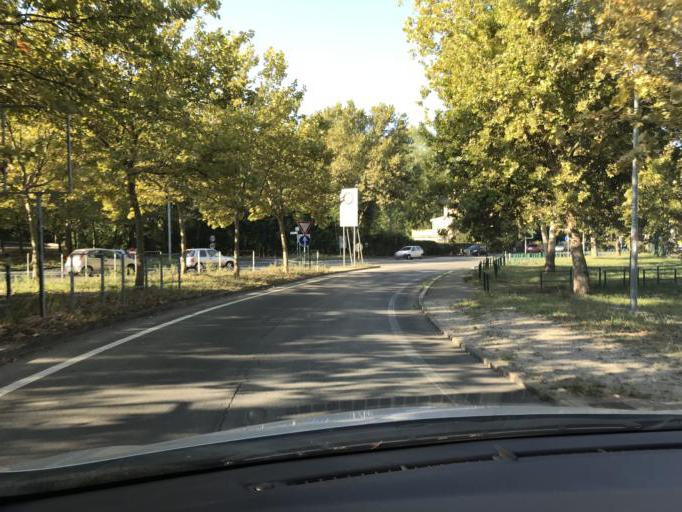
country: IT
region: Umbria
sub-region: Provincia di Perugia
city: Lacugnano
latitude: 43.1058
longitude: 12.3591
